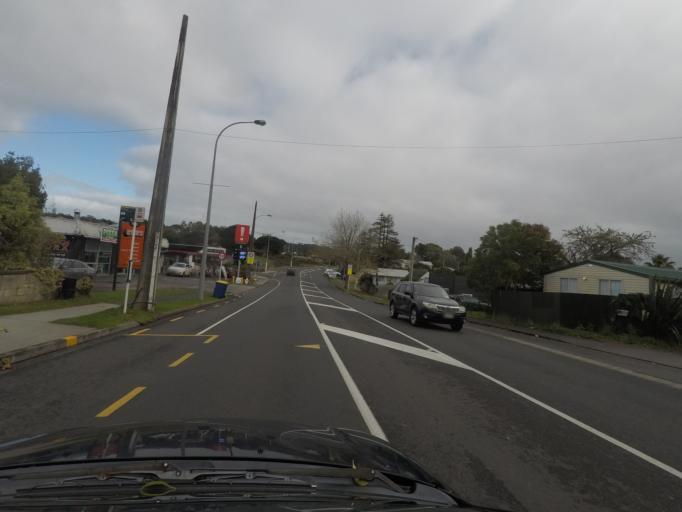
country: NZ
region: Auckland
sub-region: Auckland
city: Rosebank
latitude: -36.8658
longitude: 174.5791
